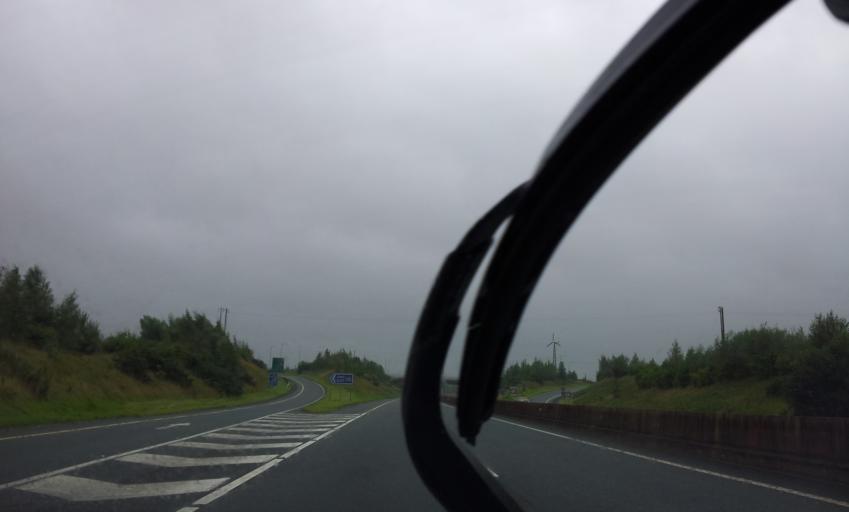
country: IE
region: Munster
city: Cahir
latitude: 52.4033
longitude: -7.9141
